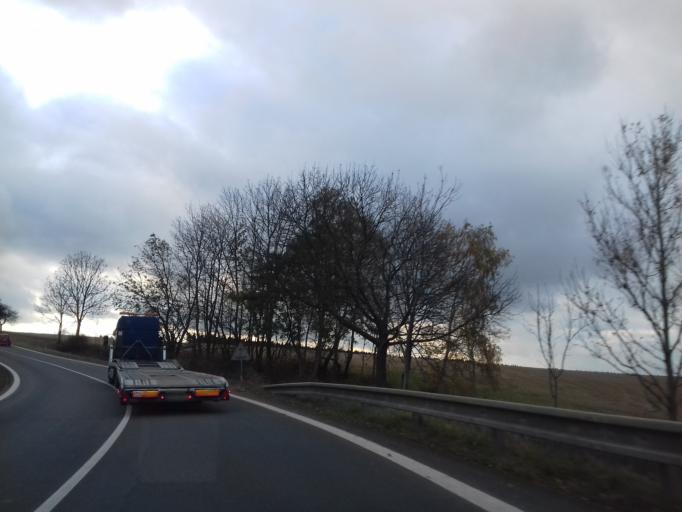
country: CZ
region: Pardubicky
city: Pomezi
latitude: 49.7323
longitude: 16.3344
